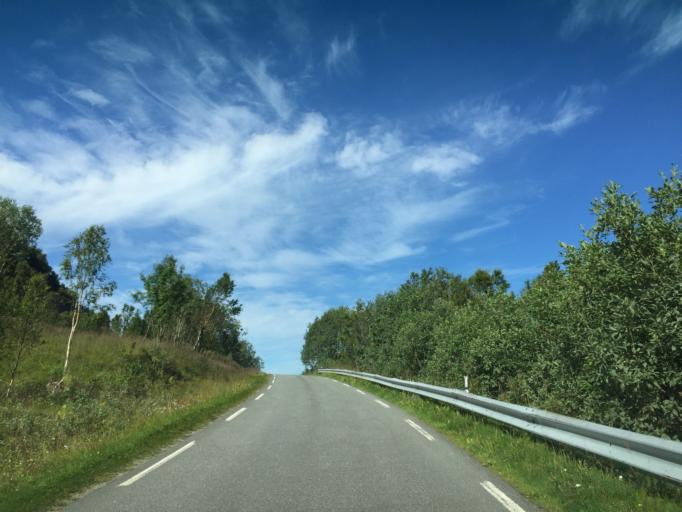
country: NO
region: Nordland
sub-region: Vagan
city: Svolvaer
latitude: 68.4006
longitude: 14.5261
